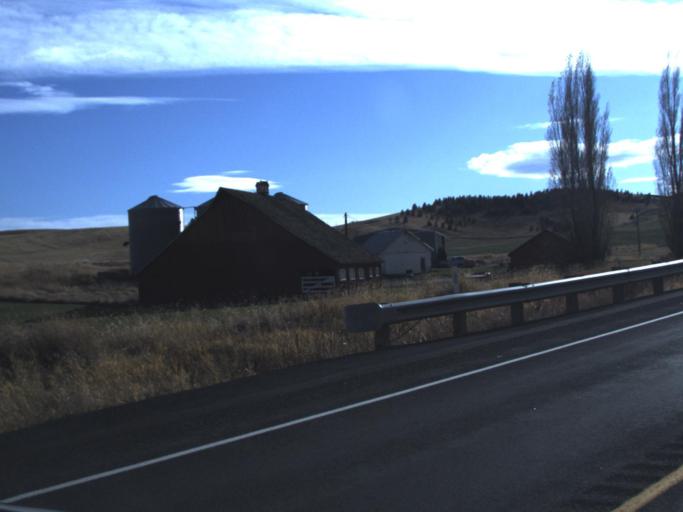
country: US
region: Washington
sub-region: Whitman County
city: Colfax
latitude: 46.8769
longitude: -117.3971
